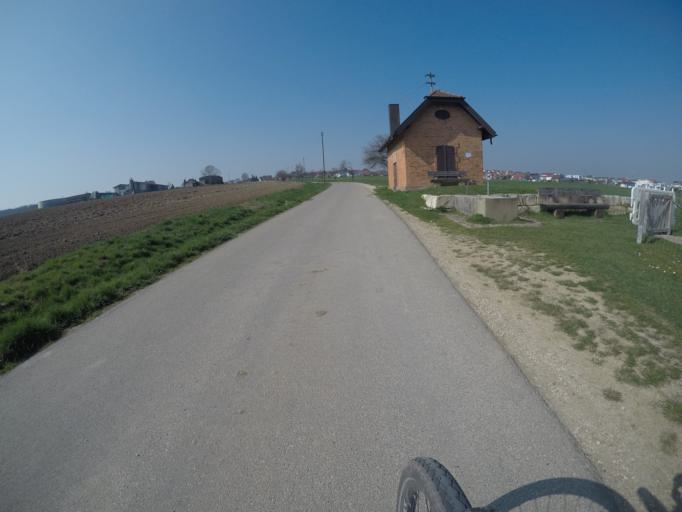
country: DE
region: Baden-Wuerttemberg
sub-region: Regierungsbezirk Stuttgart
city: Altdorf
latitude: 48.5937
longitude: 9.2806
